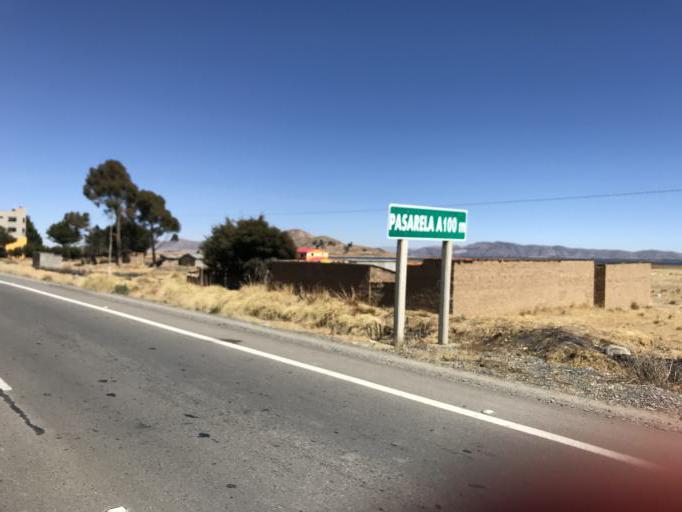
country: BO
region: La Paz
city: Huarina
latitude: -16.2097
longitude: -68.5928
